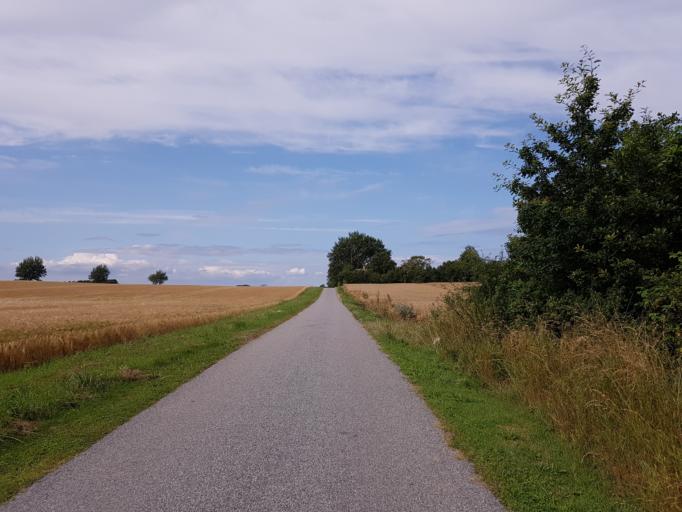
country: DK
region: Zealand
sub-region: Guldborgsund Kommune
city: Nykobing Falster
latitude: 54.5699
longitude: 11.9678
